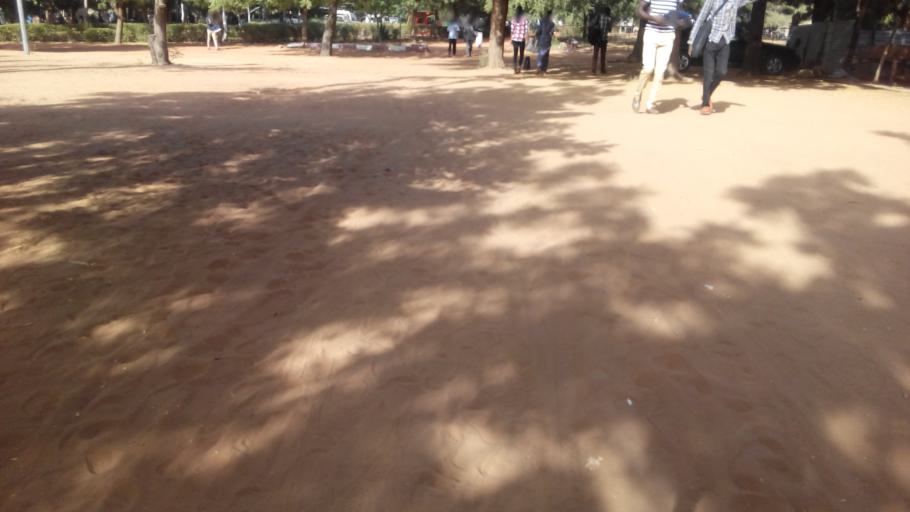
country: NE
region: Niamey
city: Niamey
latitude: 13.5021
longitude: 2.0951
